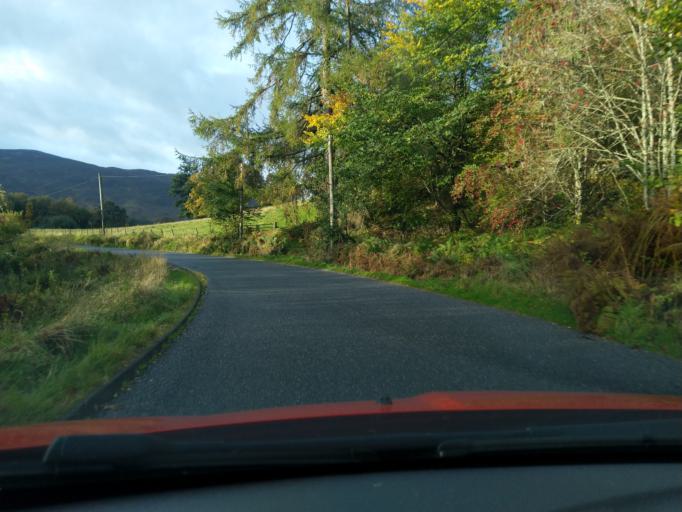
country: GB
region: Scotland
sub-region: Perth and Kinross
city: Aberfeldy
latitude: 56.7035
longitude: -4.1343
